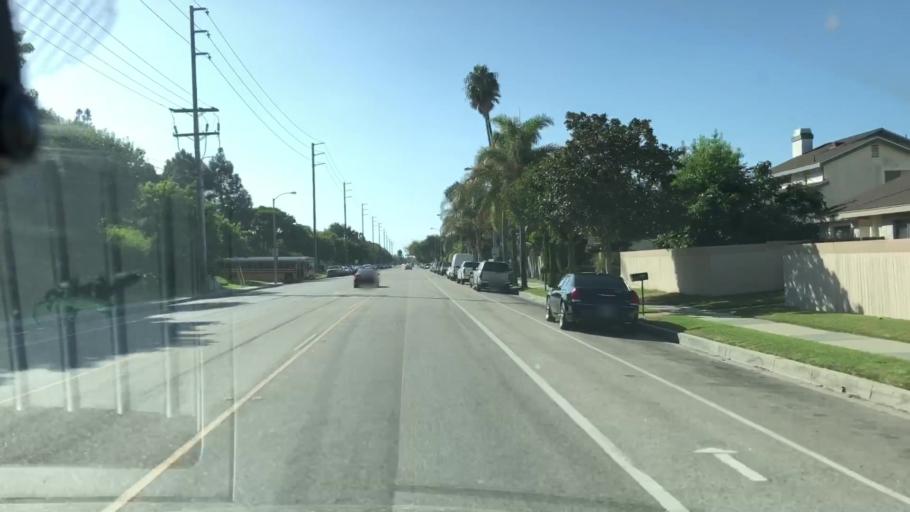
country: US
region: California
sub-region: Ventura County
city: Channel Islands Beach
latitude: 34.1813
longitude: -119.2136
